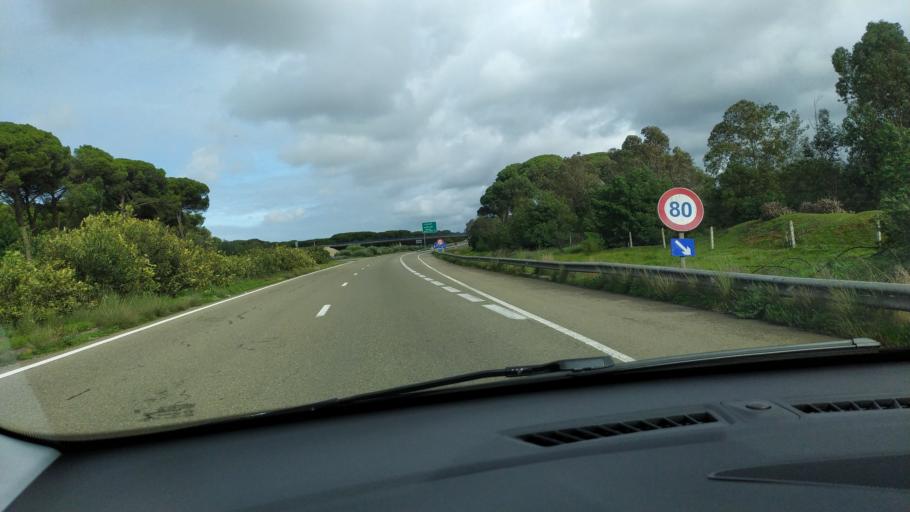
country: MA
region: Tanger-Tetouan
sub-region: Larache
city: Larache
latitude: 35.1377
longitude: -6.1467
